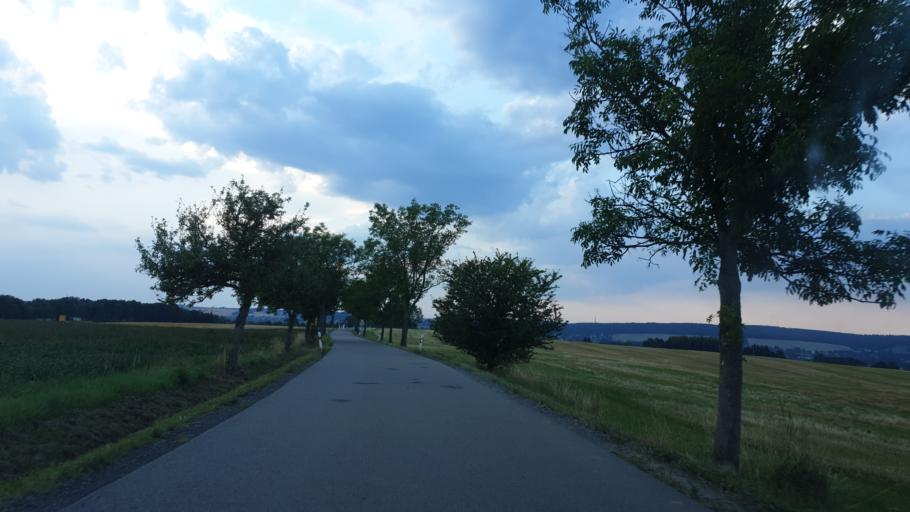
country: DE
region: Saxony
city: Niederdorf
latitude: 50.7866
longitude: 12.7967
